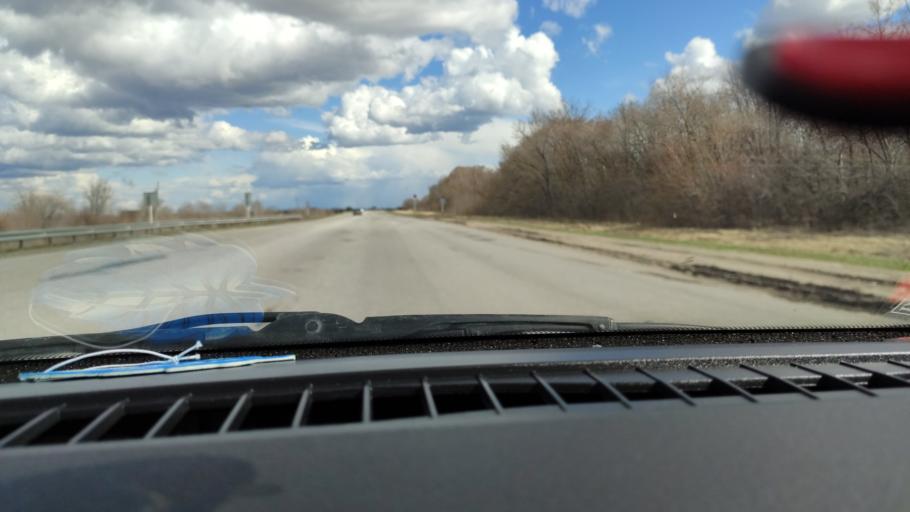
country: RU
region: Samara
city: Varlamovo
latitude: 53.1218
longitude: 48.3173
